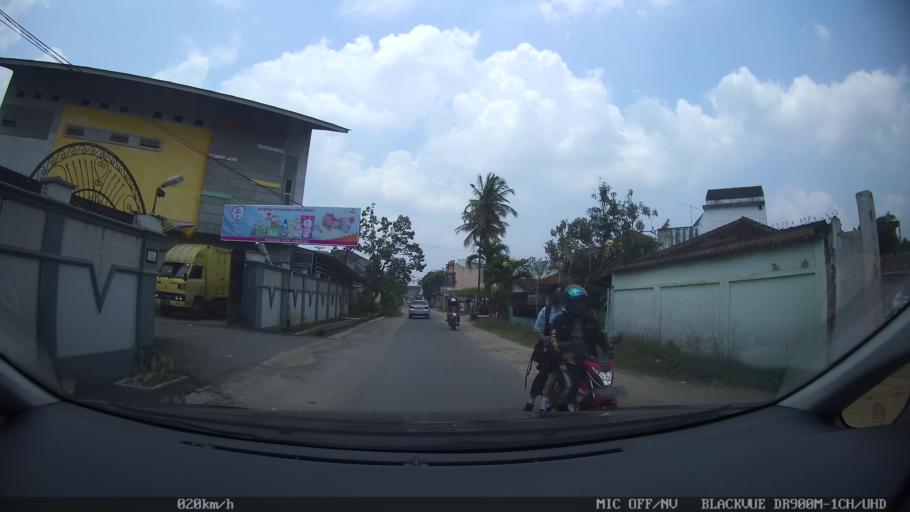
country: ID
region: Lampung
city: Pringsewu
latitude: -5.3524
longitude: 104.9779
